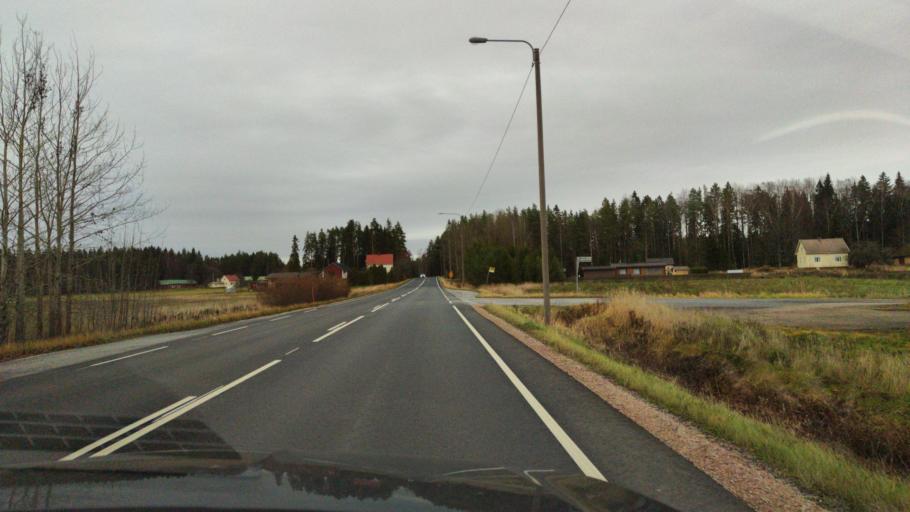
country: FI
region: Varsinais-Suomi
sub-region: Turku
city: Vahto
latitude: 60.6498
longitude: 22.4268
